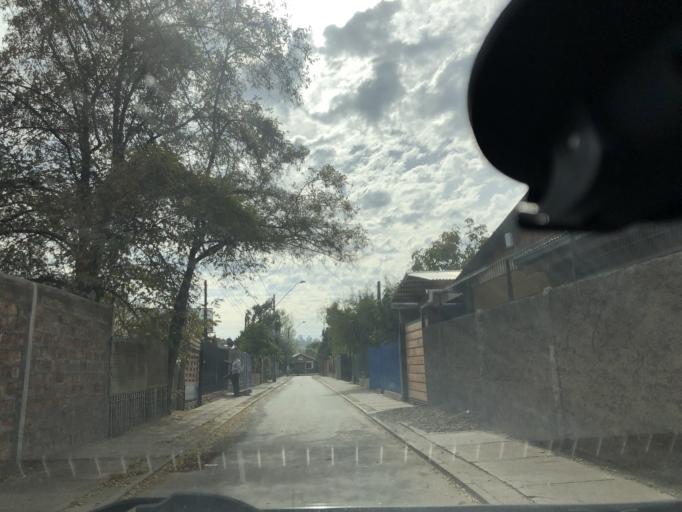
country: CL
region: Santiago Metropolitan
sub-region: Provincia de Cordillera
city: Puente Alto
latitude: -33.6107
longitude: -70.5215
